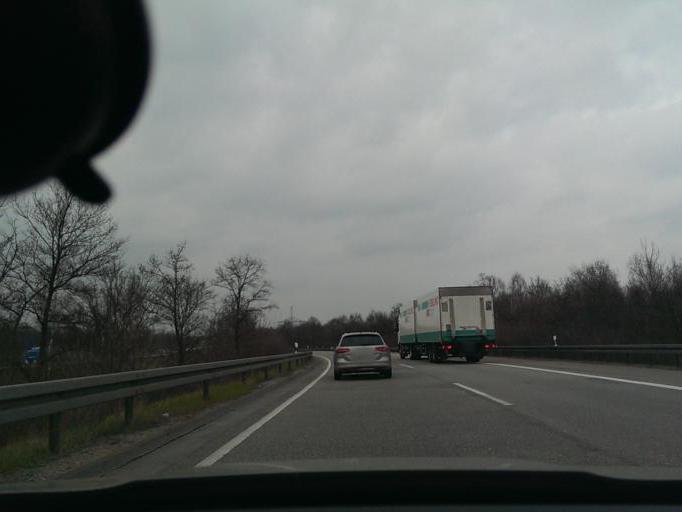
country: DE
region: Lower Saxony
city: Garbsen-Mitte
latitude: 52.4280
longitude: 9.6672
